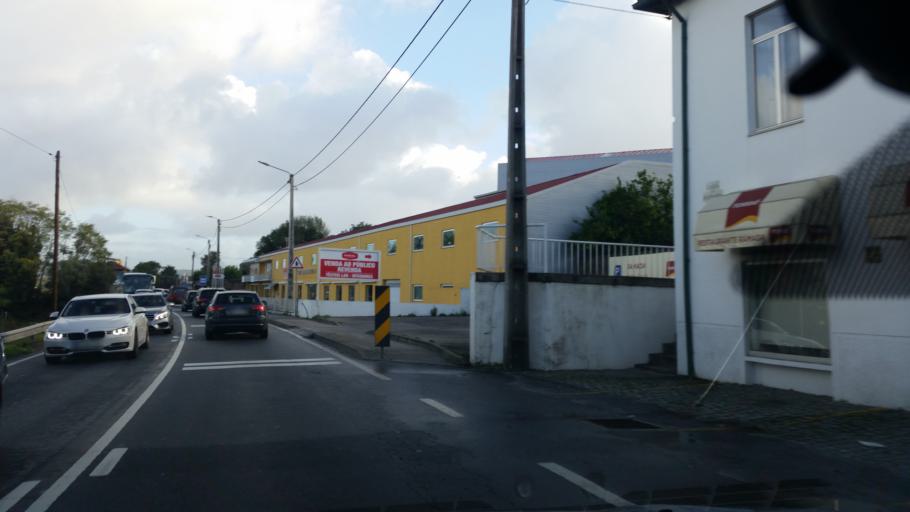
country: PT
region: Porto
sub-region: Santo Tirso
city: Sao Miguel do Couto
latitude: 41.3526
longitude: -8.4502
